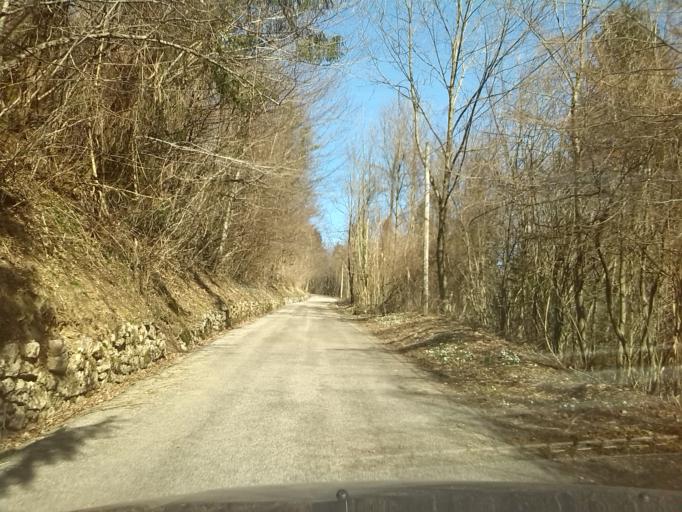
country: IT
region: Friuli Venezia Giulia
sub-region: Provincia di Udine
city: Clodig
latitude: 46.1866
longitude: 13.5835
